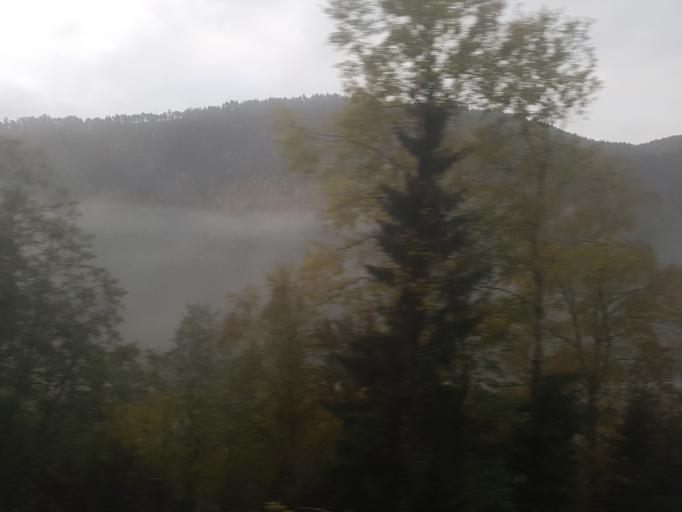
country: NO
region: Sor-Trondelag
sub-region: Midtre Gauldal
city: Storen
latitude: 62.9970
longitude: 10.2412
